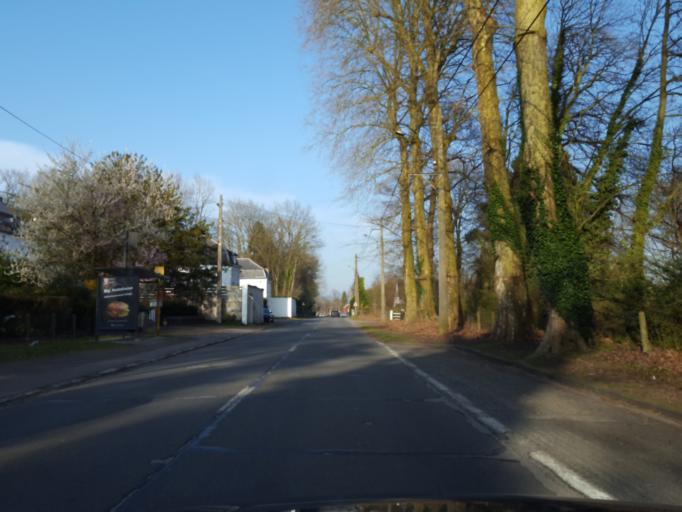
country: BE
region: Wallonia
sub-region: Province du Hainaut
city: Mons
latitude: 50.4620
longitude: 3.9959
